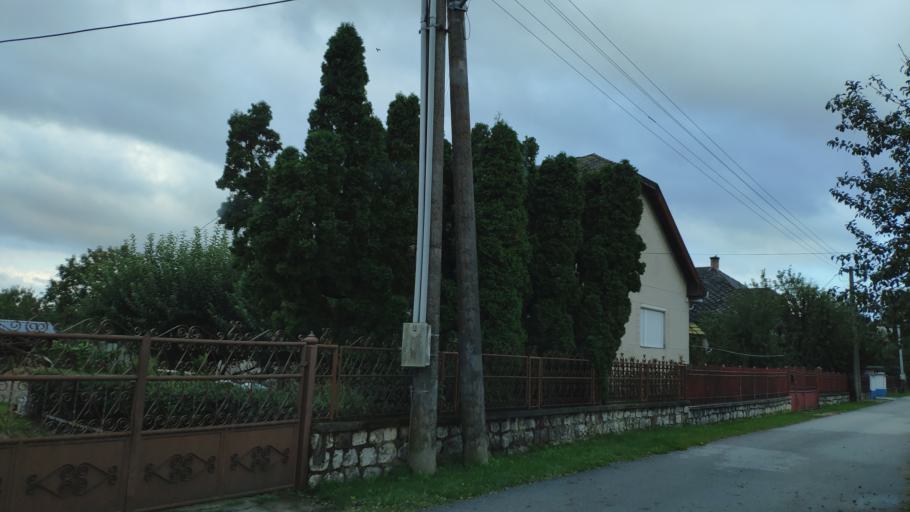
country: SK
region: Kosicky
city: Moldava nad Bodvou
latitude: 48.5774
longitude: 20.9549
